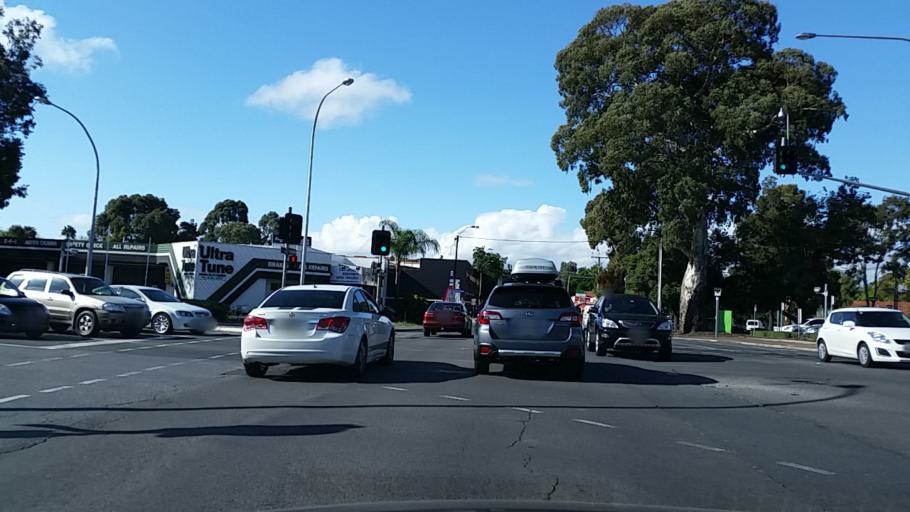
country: AU
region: South Australia
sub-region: Norwood Payneham St Peters
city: Royston Park
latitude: -34.9095
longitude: 138.6279
